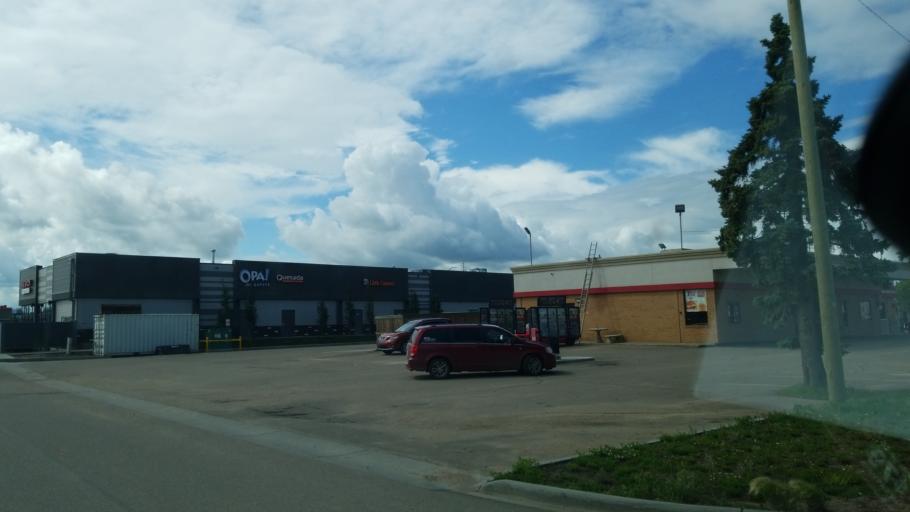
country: CA
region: Saskatchewan
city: Lloydminster
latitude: 53.2771
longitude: -110.0057
